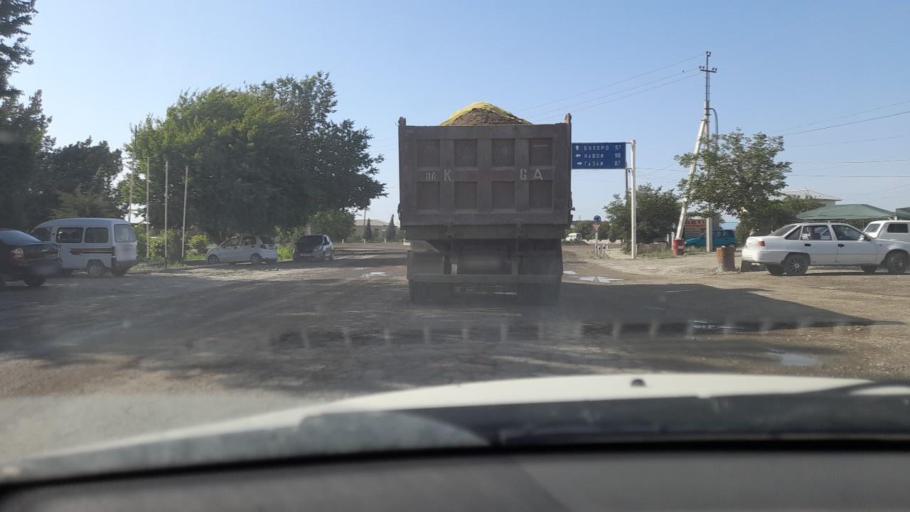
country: UZ
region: Bukhara
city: Romiton
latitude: 40.0467
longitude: 64.3288
